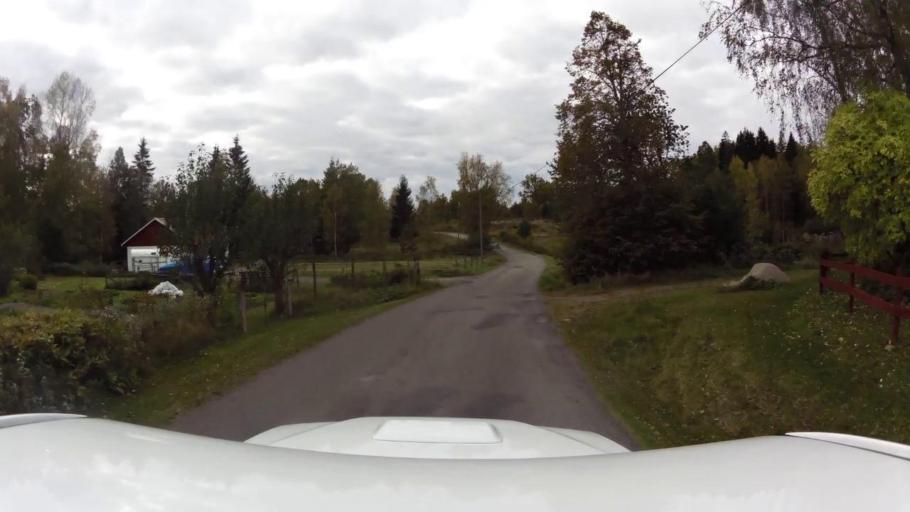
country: SE
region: OEstergoetland
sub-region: Kinda Kommun
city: Rimforsa
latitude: 58.2296
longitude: 15.6256
